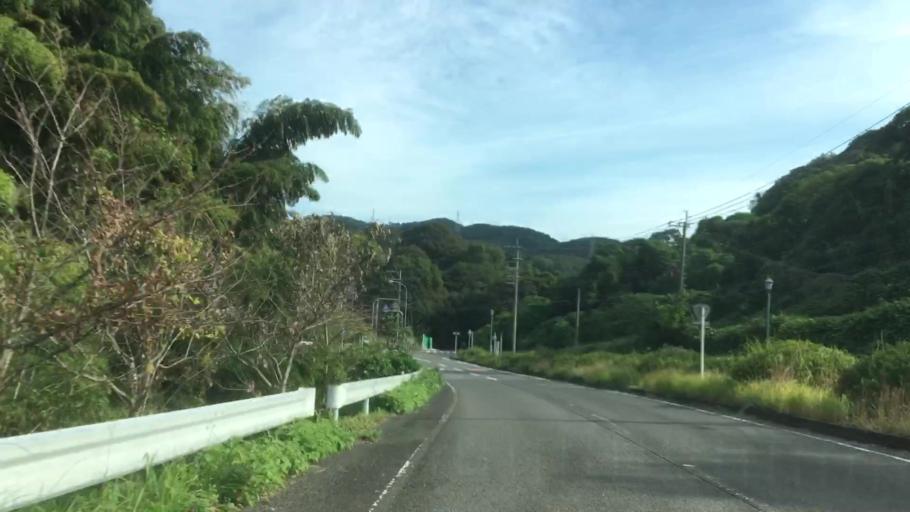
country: JP
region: Nagasaki
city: Sasebo
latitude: 32.9972
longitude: 129.6582
